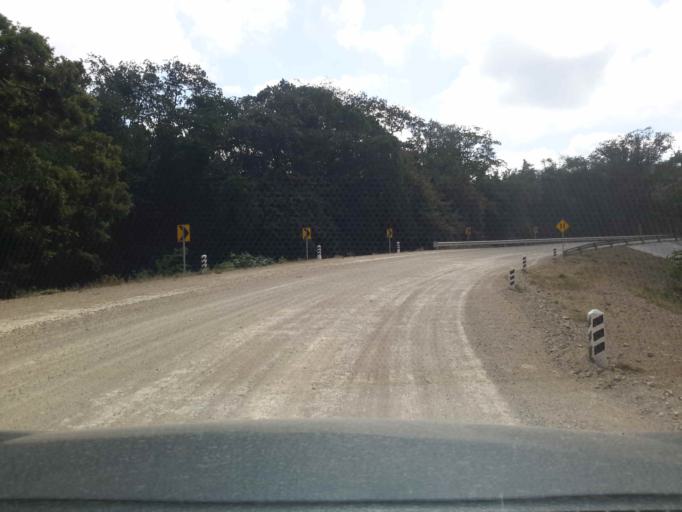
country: NI
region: Rivas
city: San Juan del Sur
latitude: 11.1762
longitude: -85.8009
